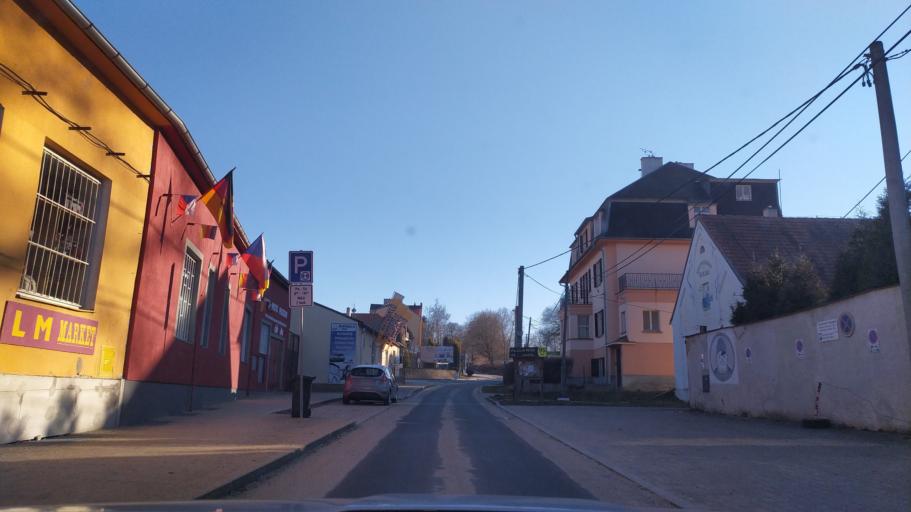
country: CZ
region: Karlovarsky
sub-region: Okres Cheb
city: Frantiskovy Lazne
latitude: 50.1133
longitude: 12.3502
